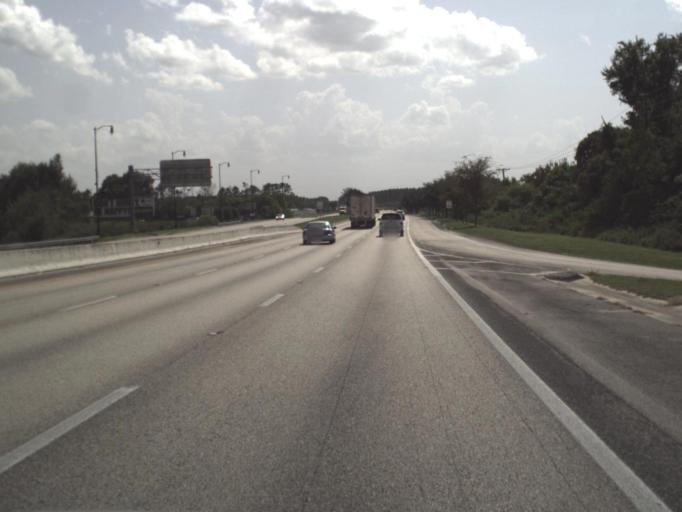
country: US
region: Florida
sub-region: Polk County
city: Haines City
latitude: 28.1048
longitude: -81.6439
